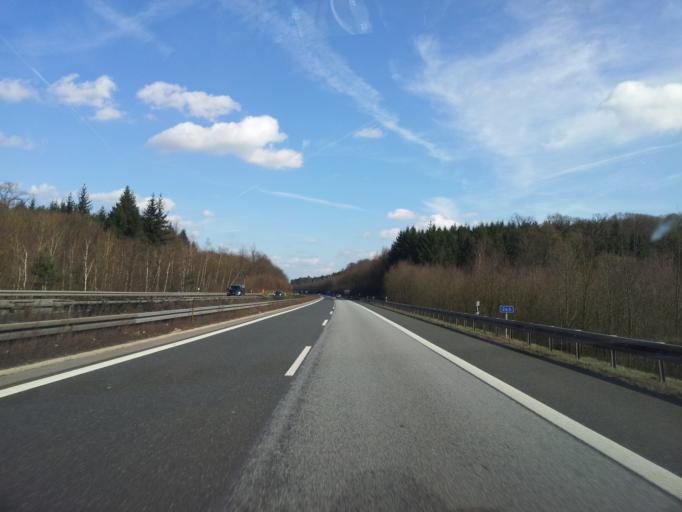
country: DE
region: Bavaria
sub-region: Regierungsbezirk Unterfranken
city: Donnersdorf
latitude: 50.0043
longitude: 10.3942
